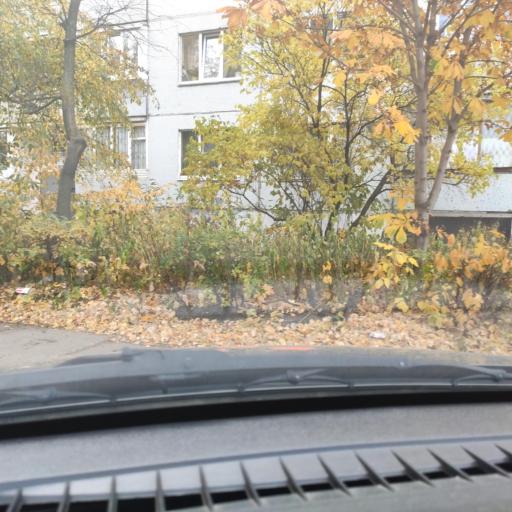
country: RU
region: Samara
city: Tol'yatti
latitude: 53.5300
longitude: 49.3102
